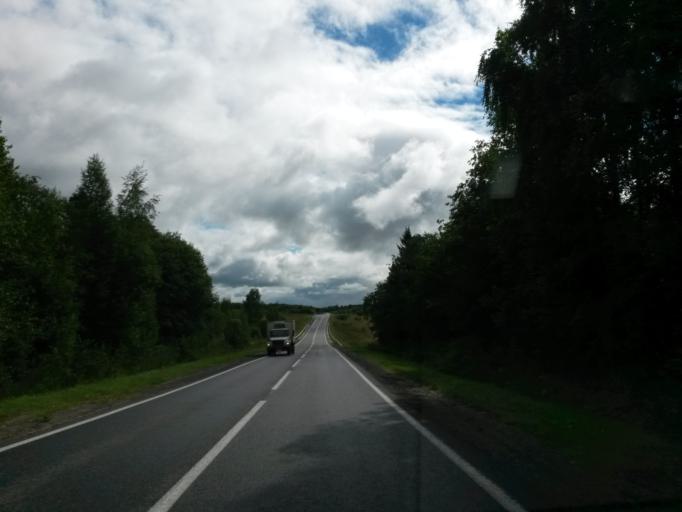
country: RU
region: Jaroslavl
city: Konstantinovskiy
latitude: 57.8150
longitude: 39.7176
